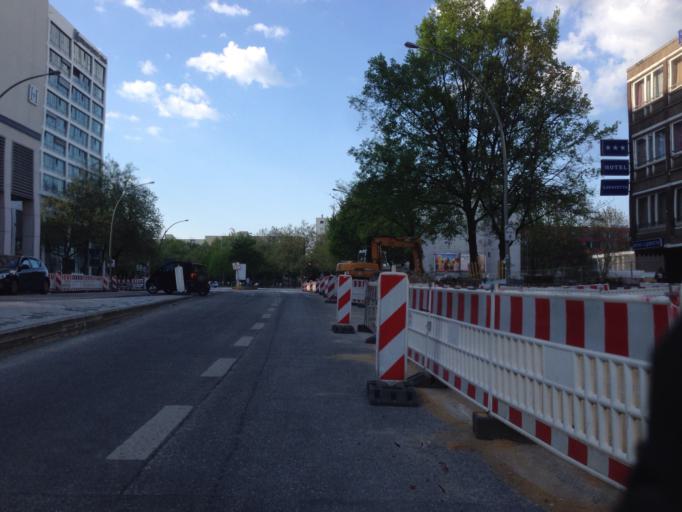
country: DE
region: Hamburg
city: St. Pauli
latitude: 53.5502
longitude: 9.9557
